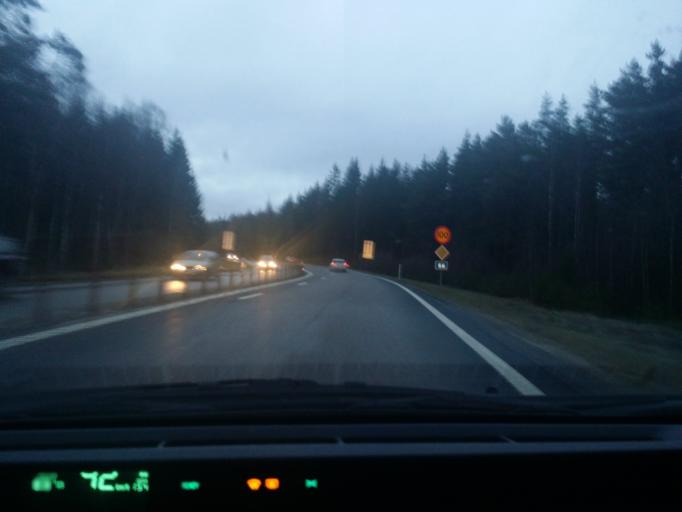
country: SE
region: Soedermanland
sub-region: Eskilstuna Kommun
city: Hallbybrunn
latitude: 59.4094
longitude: 16.3715
